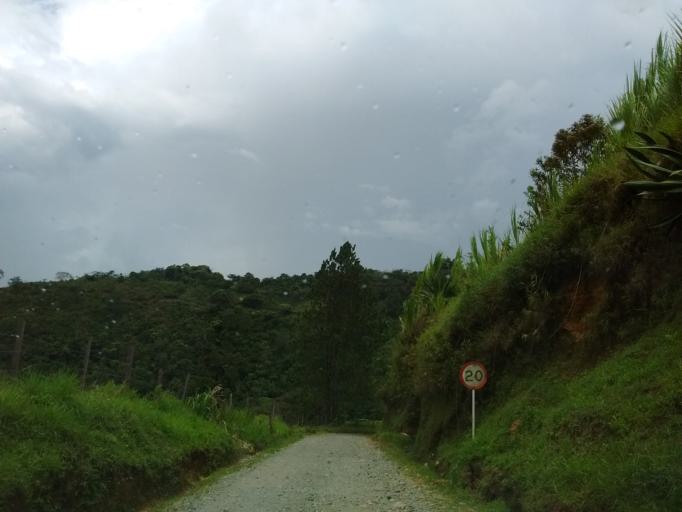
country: CO
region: Cauca
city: Cajibio
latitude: 2.5605
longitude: -76.6329
